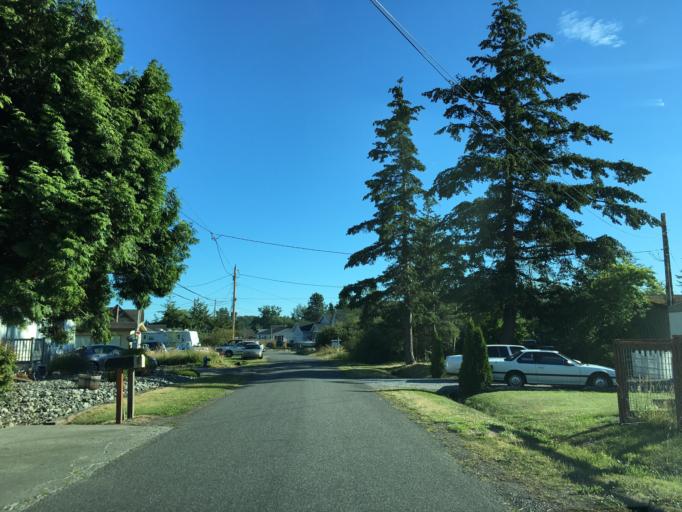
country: US
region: Washington
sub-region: Whatcom County
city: Birch Bay
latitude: 48.9118
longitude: -122.7473
